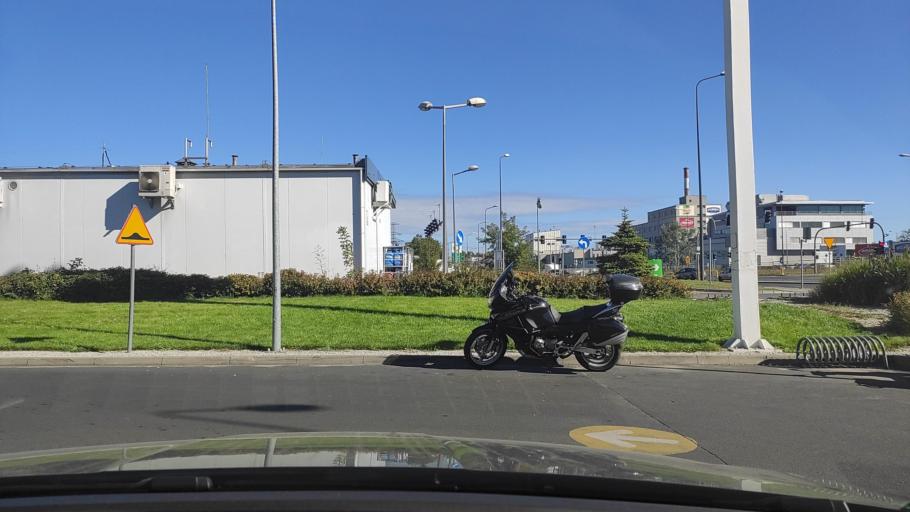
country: PL
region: Greater Poland Voivodeship
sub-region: Powiat poznanski
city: Czerwonak
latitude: 52.4257
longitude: 16.9774
